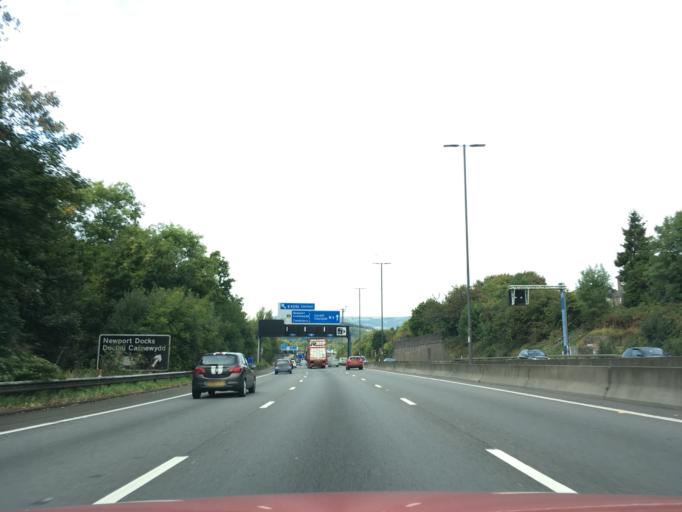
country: GB
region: Wales
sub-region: Newport
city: Caerleon
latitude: 51.6004
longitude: -2.9708
